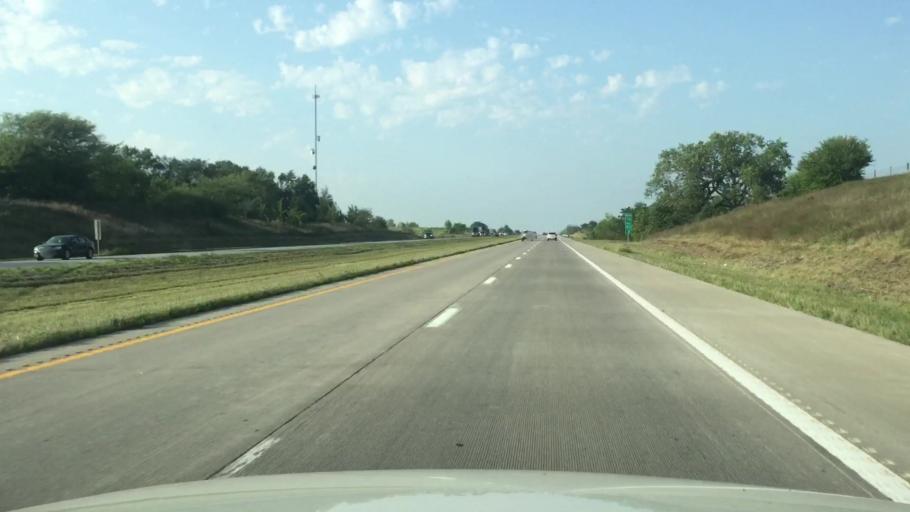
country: US
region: Missouri
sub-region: Clinton County
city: Lathrop
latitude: 39.6045
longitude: -94.2522
